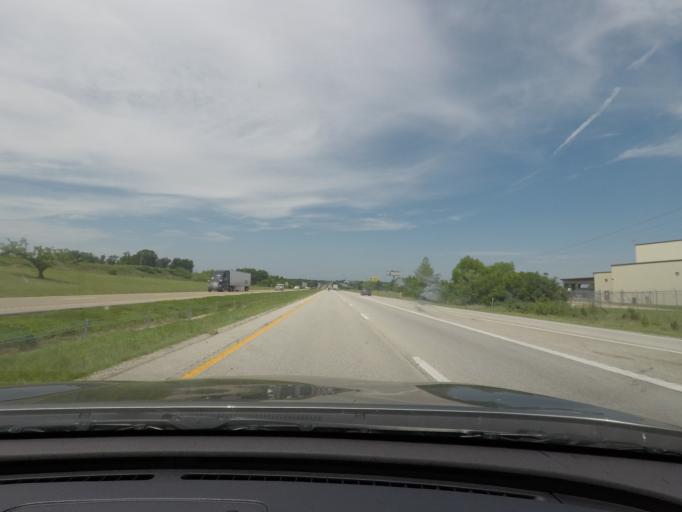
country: US
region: Missouri
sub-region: Cooper County
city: Boonville
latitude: 38.9358
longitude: -92.7792
